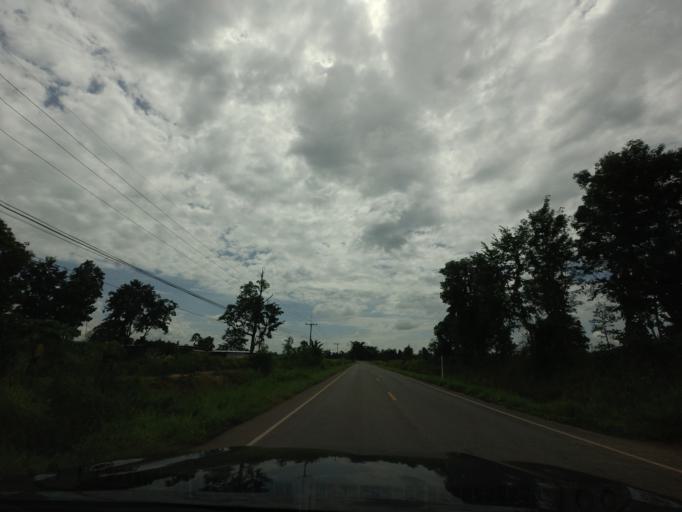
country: TH
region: Changwat Udon Thani
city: Nam Som
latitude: 17.8224
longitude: 102.2705
